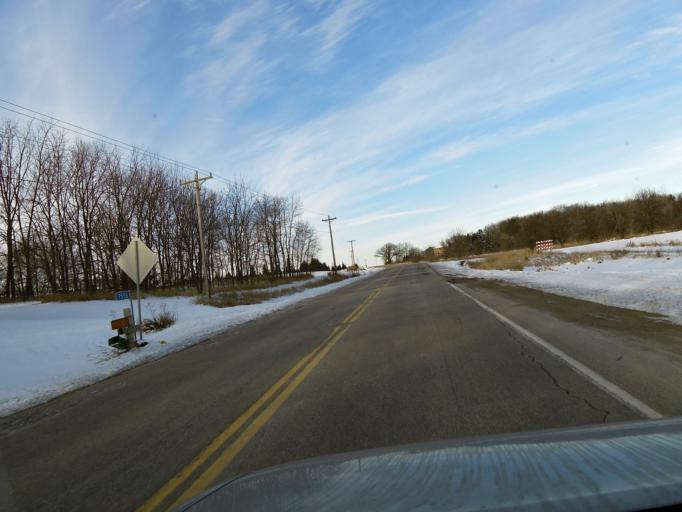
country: US
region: Minnesota
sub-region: Scott County
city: Prior Lake
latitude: 44.7658
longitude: -93.4232
